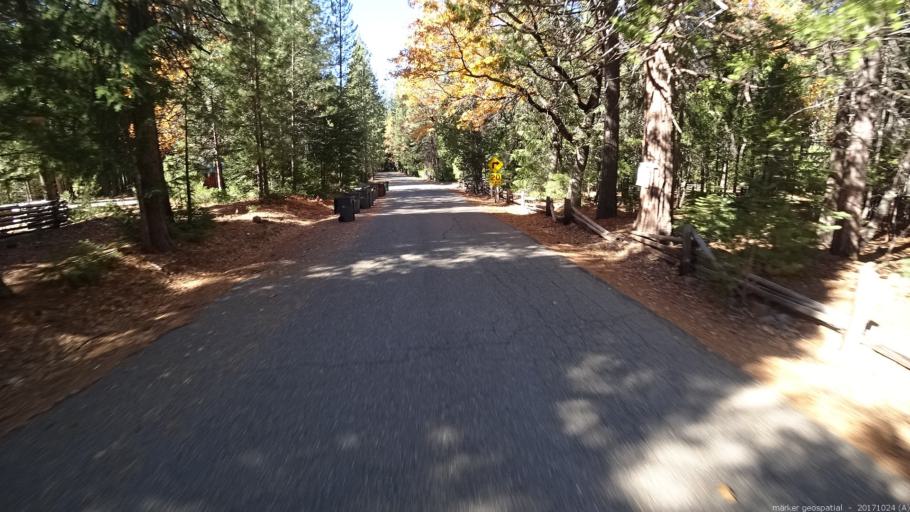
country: US
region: California
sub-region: Shasta County
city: Shingletown
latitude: 40.5141
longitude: -121.6732
